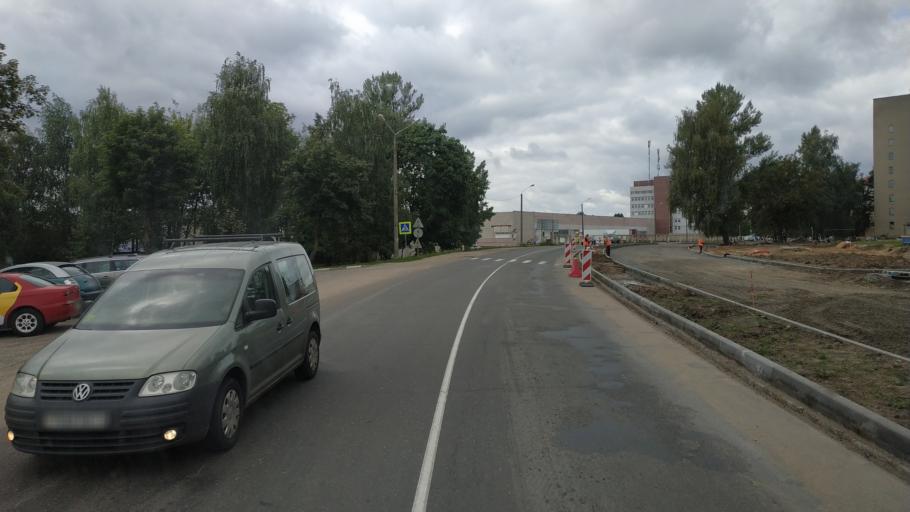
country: BY
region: Mogilev
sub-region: Mahilyowski Rayon
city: Veyno
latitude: 53.8798
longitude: 30.4098
